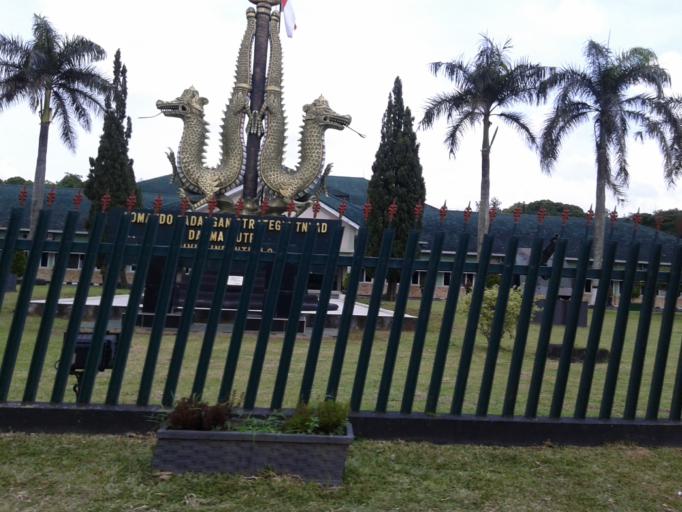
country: ID
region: East Java
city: Singosari
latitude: -7.8818
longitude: 112.6738
